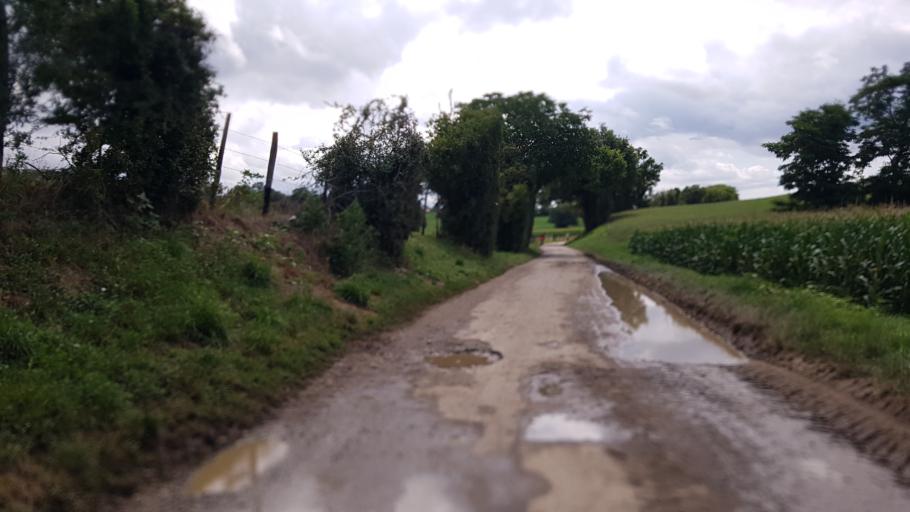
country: FR
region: Rhone-Alpes
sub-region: Departement du Rhone
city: Genas
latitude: 45.7387
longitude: 4.9912
